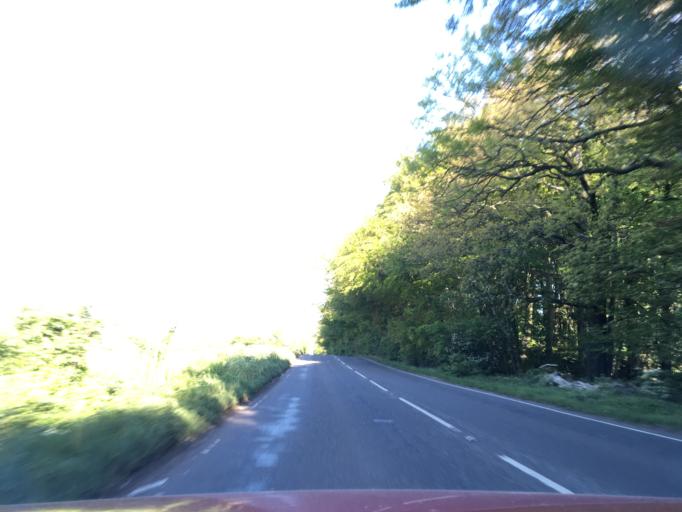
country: GB
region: England
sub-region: North Somerset
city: Easton-in-Gordano
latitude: 51.4465
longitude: -2.7085
